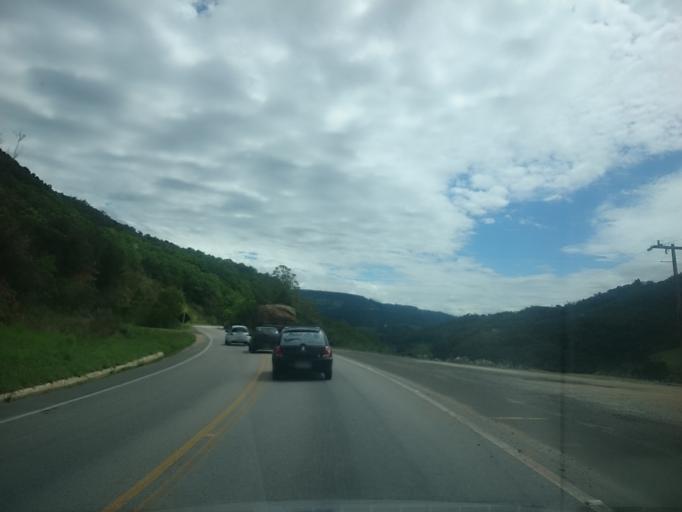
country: BR
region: Santa Catarina
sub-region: Anitapolis
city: Anitapolis
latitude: -27.6942
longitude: -49.3124
